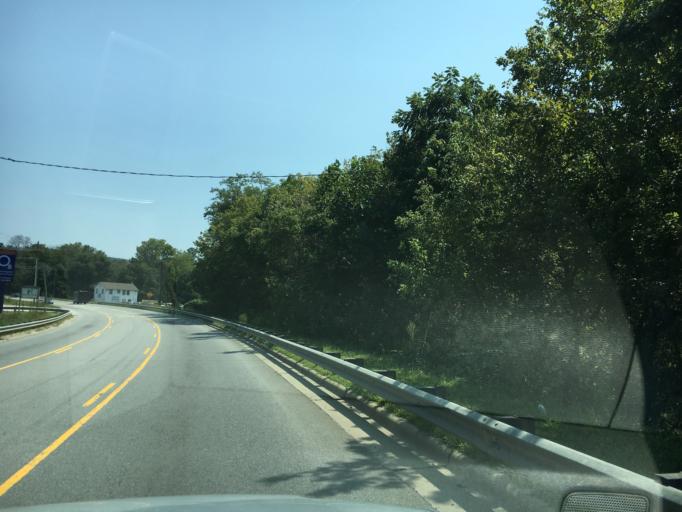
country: US
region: North Carolina
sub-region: McDowell County
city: Marion
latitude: 35.6612
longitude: -81.9722
